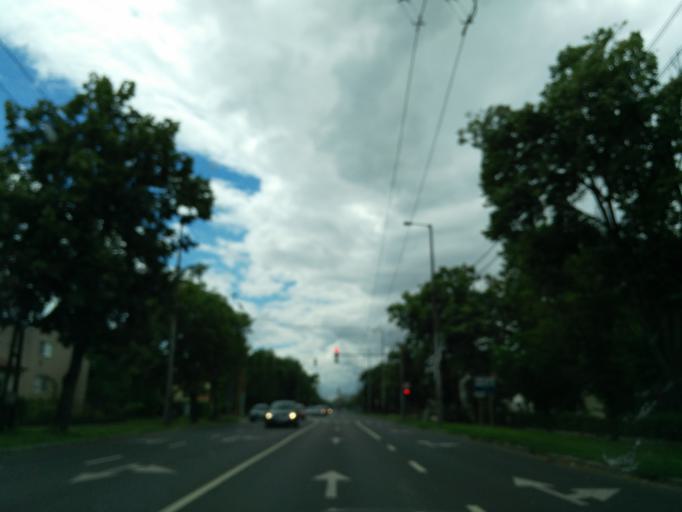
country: HU
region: Hajdu-Bihar
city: Debrecen
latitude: 47.5471
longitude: 21.6451
